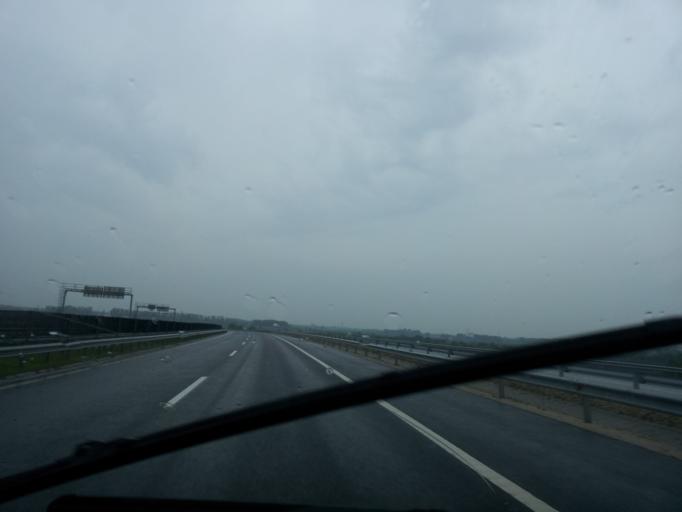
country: HU
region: Tolna
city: Tolna
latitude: 46.3832
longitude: 18.7549
